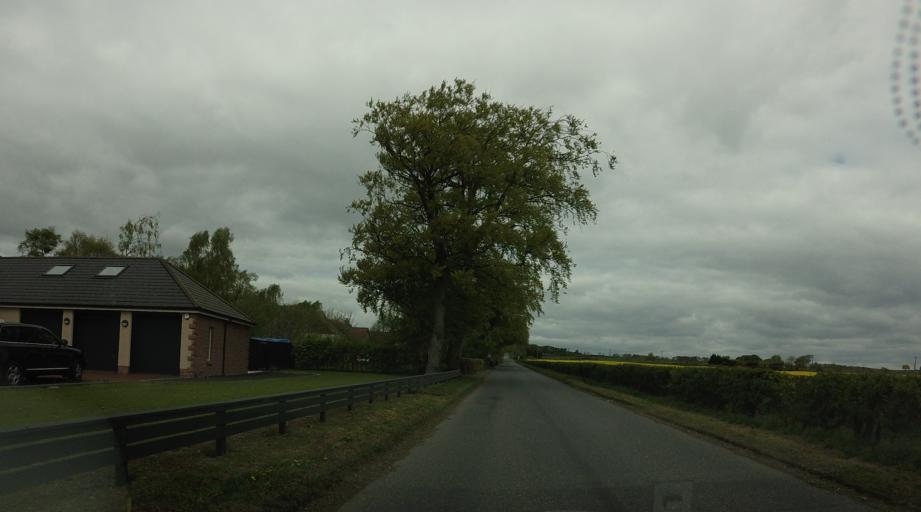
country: GB
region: Scotland
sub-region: Perth and Kinross
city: Milnathort
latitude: 56.2421
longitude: -3.3725
